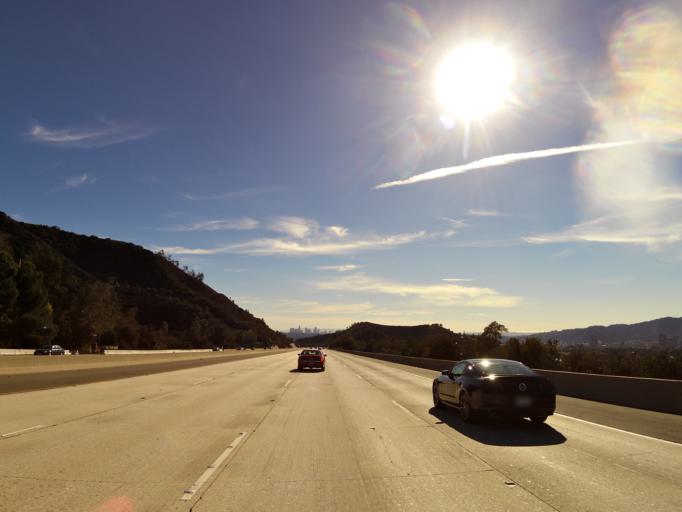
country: US
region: California
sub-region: Los Angeles County
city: La Canada Flintridge
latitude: 34.1746
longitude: -118.2218
